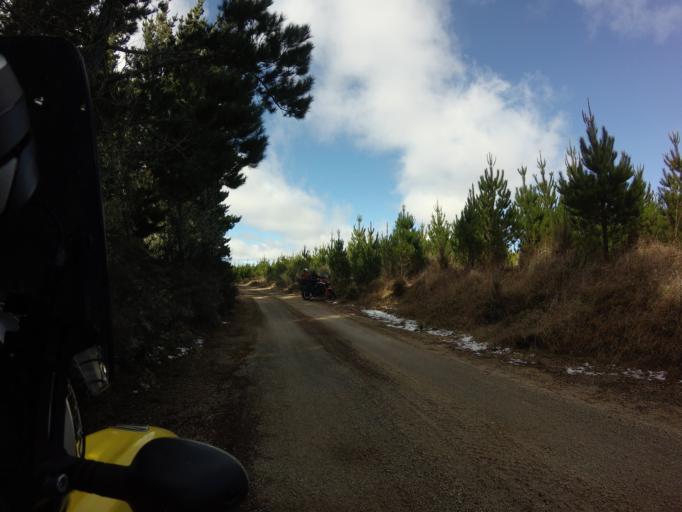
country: NZ
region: Bay of Plenty
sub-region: Whakatane District
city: Murupara
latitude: -38.8197
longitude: 176.5640
